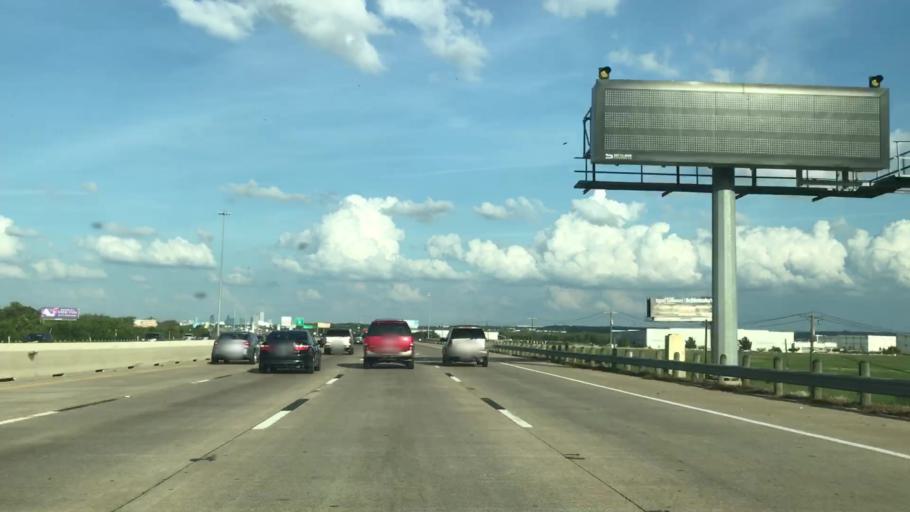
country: US
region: Texas
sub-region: Dallas County
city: Grand Prairie
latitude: 32.7621
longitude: -96.9520
